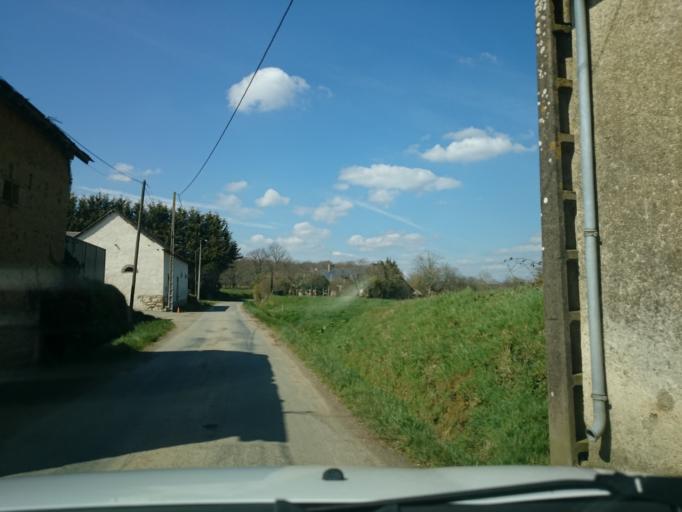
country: FR
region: Brittany
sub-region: Departement d'Ille-et-Vilaine
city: Acigne
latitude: 48.1622
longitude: -1.5200
